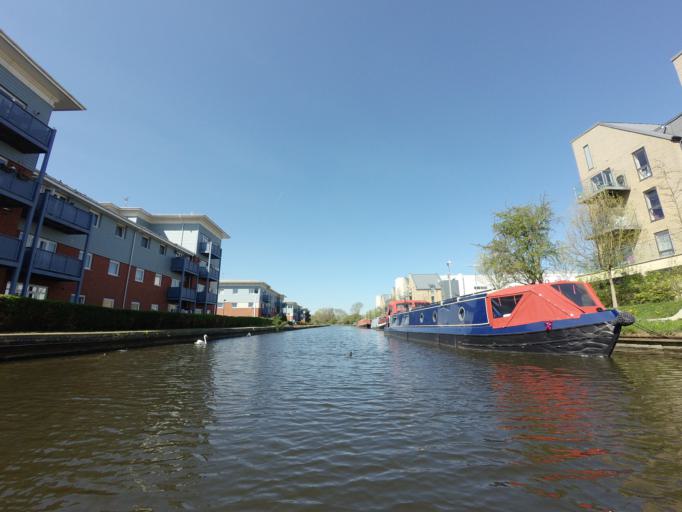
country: GB
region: England
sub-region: Greater London
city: West Drayton
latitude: 51.5144
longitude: -0.4777
